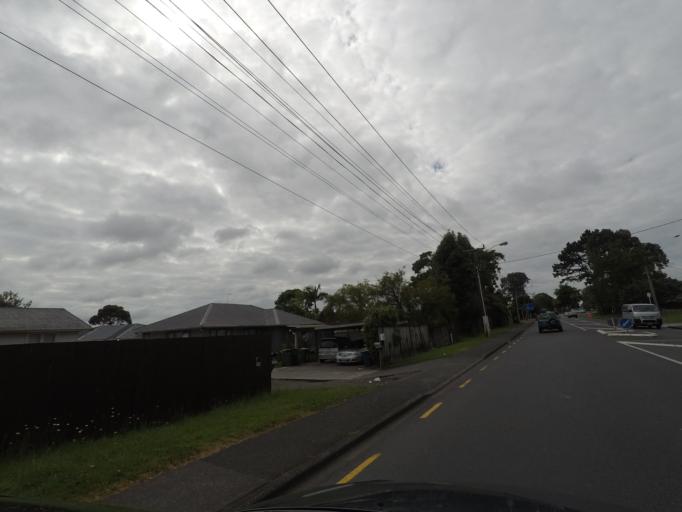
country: NZ
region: Auckland
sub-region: Auckland
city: Rosebank
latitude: -36.8593
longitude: 174.6103
